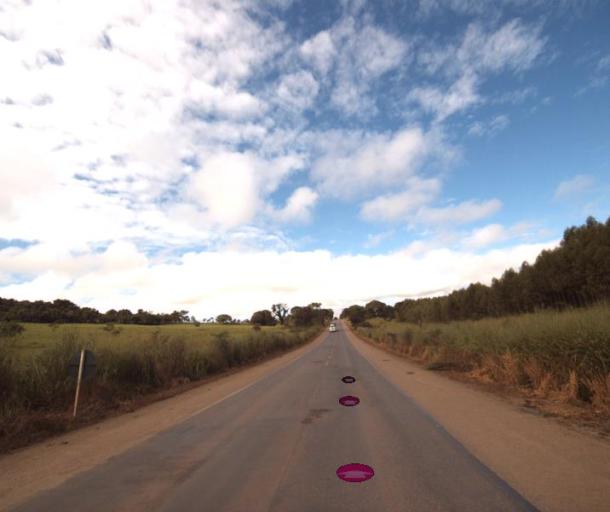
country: BR
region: Goias
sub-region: Uruacu
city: Uruacu
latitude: -14.7404
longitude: -49.2459
